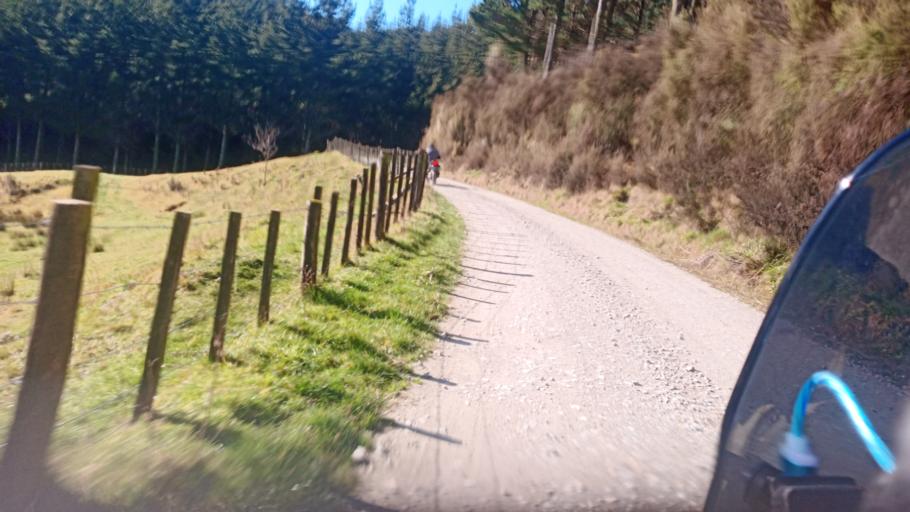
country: NZ
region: Hawke's Bay
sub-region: Wairoa District
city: Wairoa
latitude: -38.6573
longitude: 177.4919
